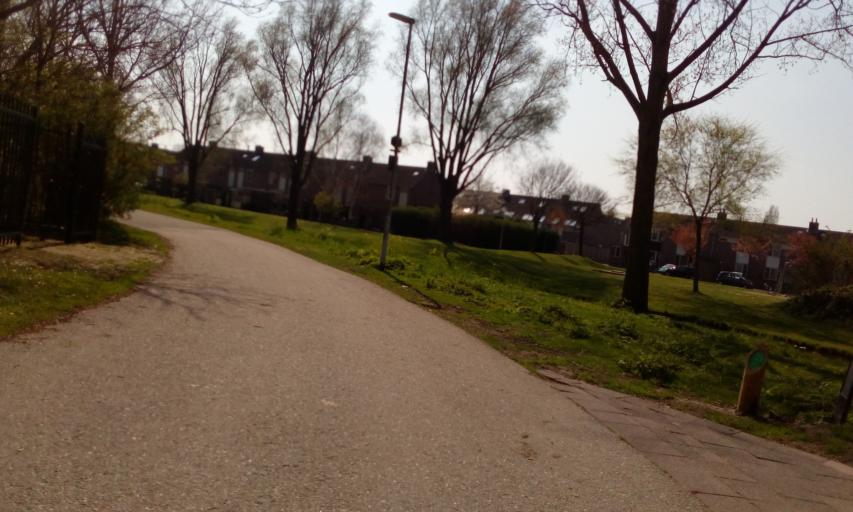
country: NL
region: South Holland
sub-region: Gemeente Spijkenisse
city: Spijkenisse
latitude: 51.8301
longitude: 4.3153
